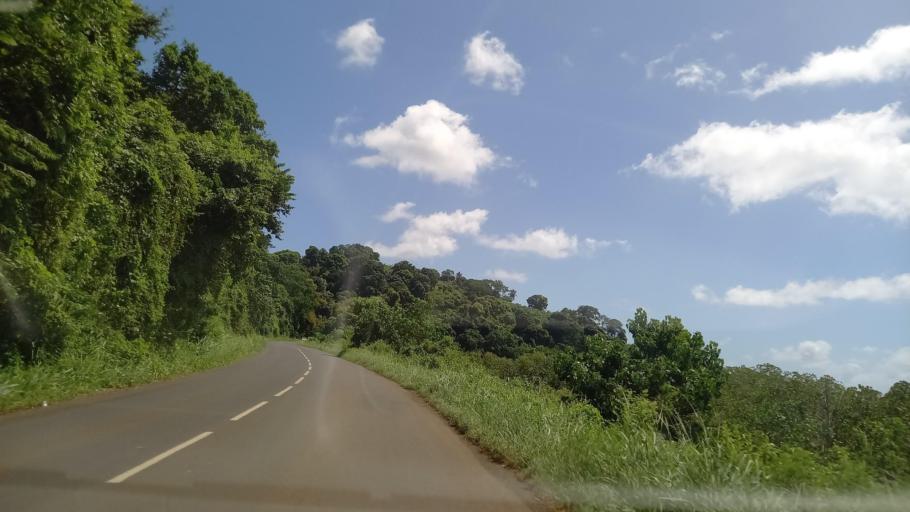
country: YT
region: Bandraboua
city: Bandraboua
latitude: -12.7215
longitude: 45.1304
